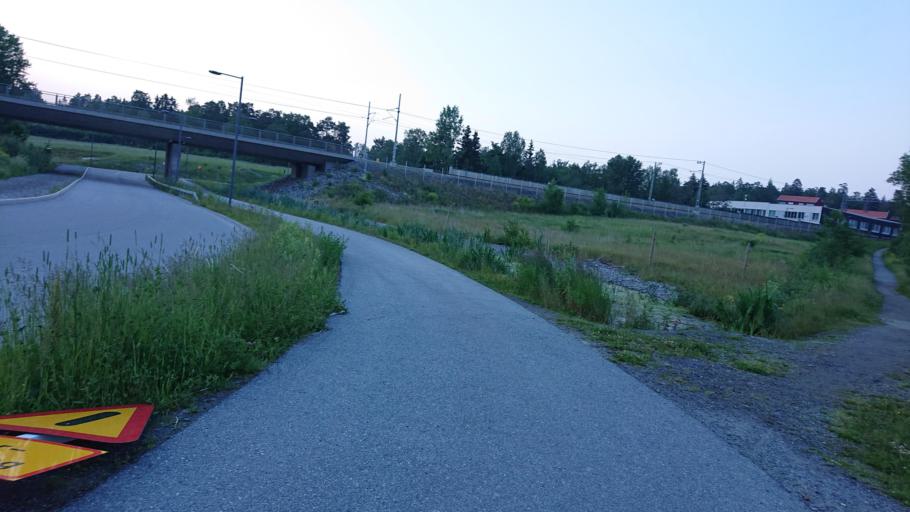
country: SE
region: Stockholm
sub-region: Osterakers Kommun
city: Akersberga
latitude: 59.4757
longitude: 18.2474
